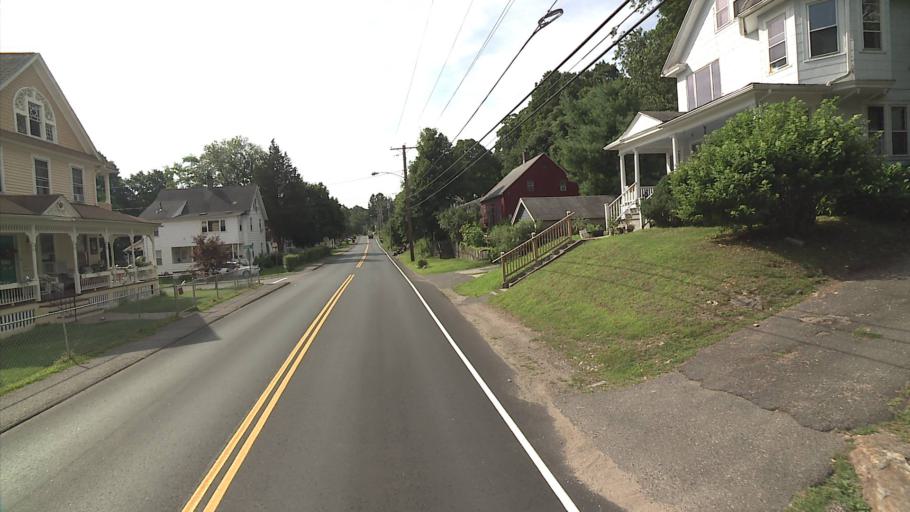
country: US
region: Connecticut
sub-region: New Haven County
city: Seymour
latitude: 41.3877
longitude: -73.0705
